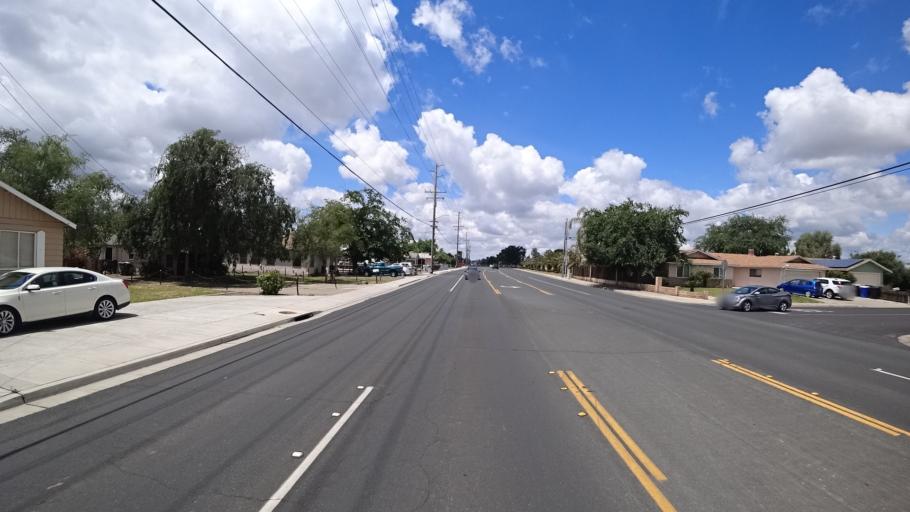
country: US
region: California
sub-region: Kings County
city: Hanford
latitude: 36.3426
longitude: -119.6302
